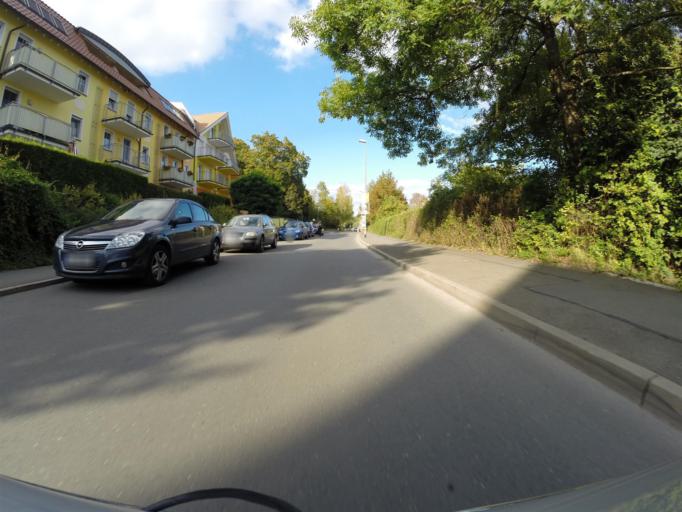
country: DE
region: Thuringia
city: Jena
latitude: 50.9480
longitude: 11.5952
